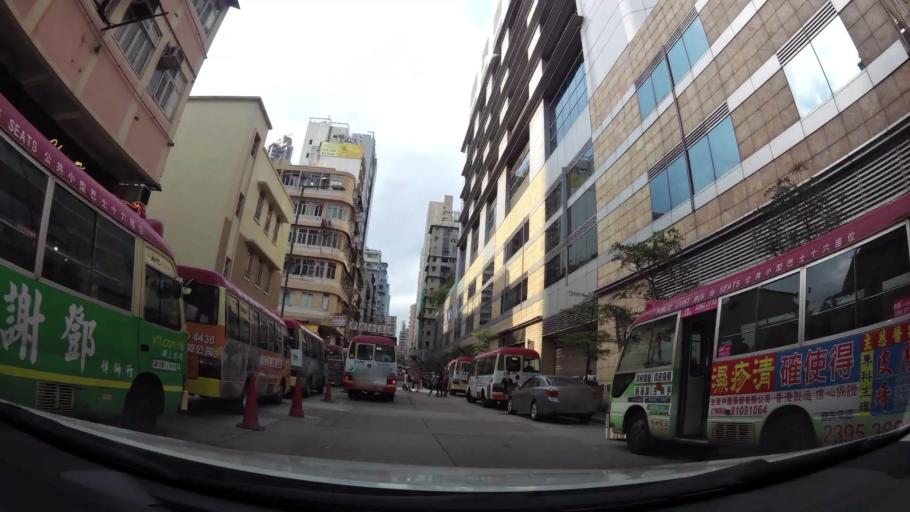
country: HK
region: Sham Shui Po
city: Sham Shui Po
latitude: 22.3177
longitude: 114.1680
